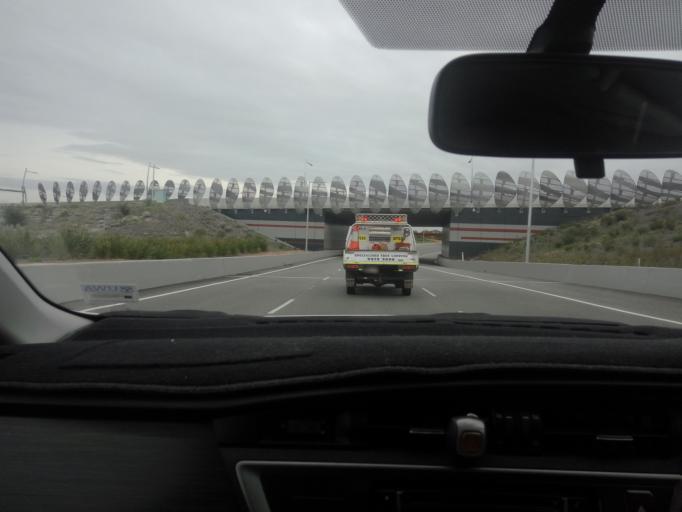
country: AU
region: Western Australia
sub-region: Belmont
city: Kewdale
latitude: -31.9626
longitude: 115.9553
